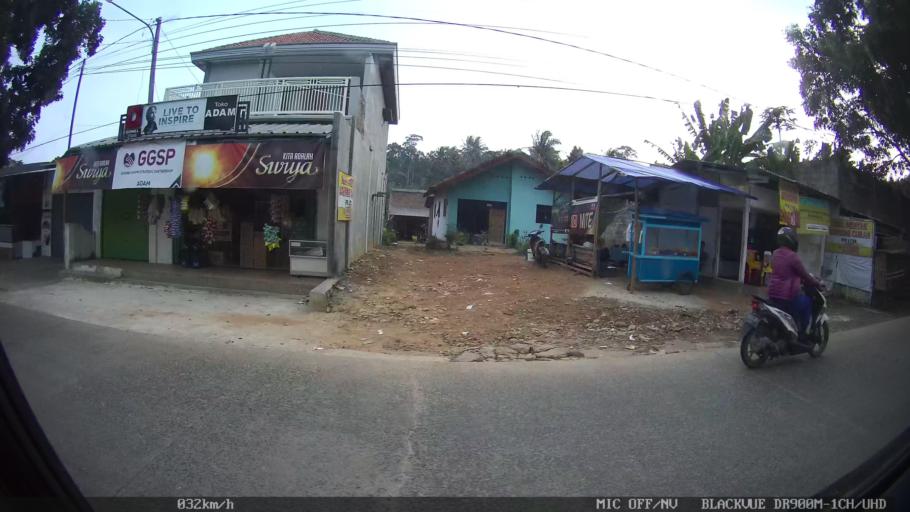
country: ID
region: Lampung
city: Bandarlampung
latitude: -5.4082
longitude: 105.2215
